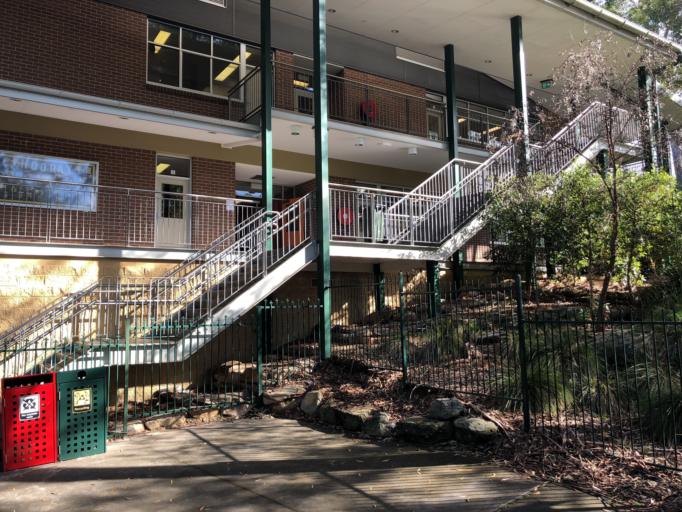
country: AU
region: New South Wales
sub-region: The Hills Shire
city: Glenhaven
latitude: -33.6841
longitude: 151.0128
